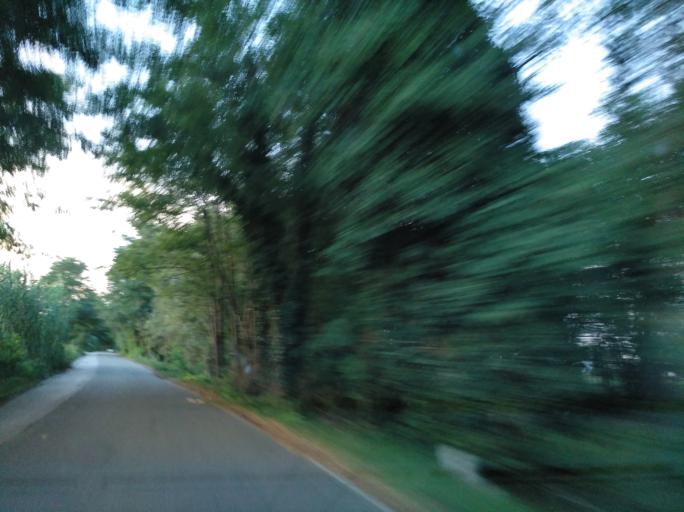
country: ES
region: Catalonia
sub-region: Provincia de Girona
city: Salt
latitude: 41.9603
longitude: 2.7966
